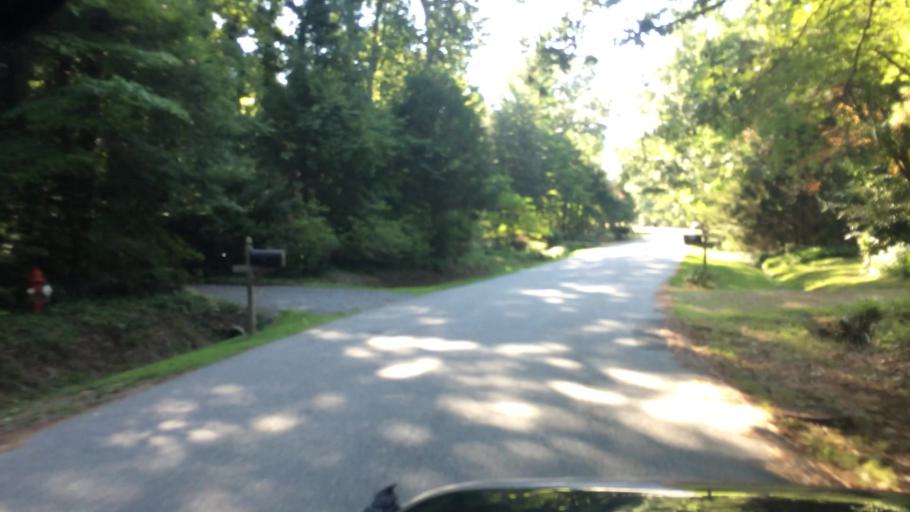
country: US
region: Virginia
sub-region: James City County
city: Williamsburg
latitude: 37.2357
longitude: -76.7997
